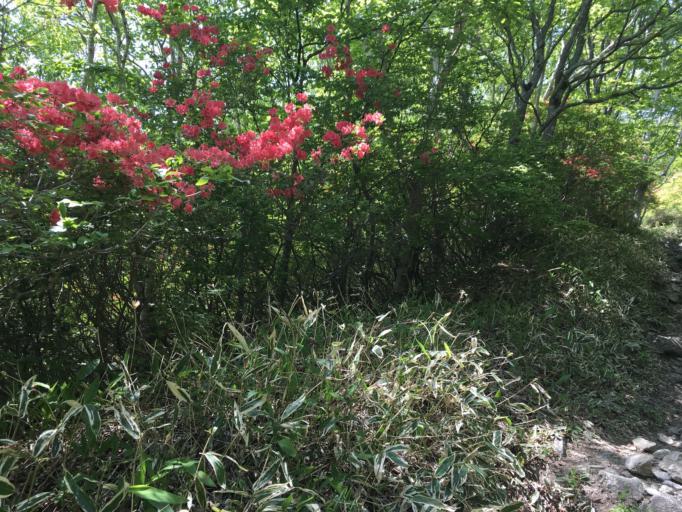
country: JP
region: Iwate
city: Ofunato
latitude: 39.1805
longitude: 141.7400
